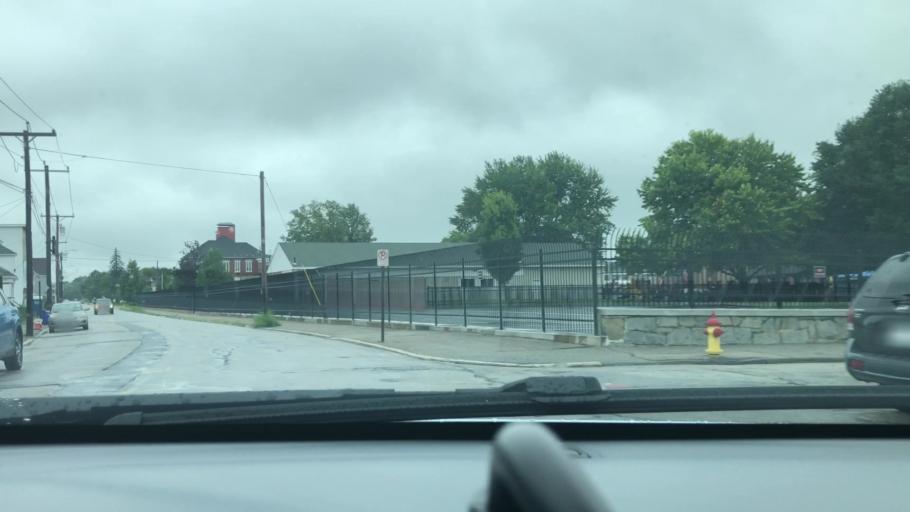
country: US
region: New Hampshire
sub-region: Hillsborough County
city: Pinardville
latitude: 42.9939
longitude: -71.4816
